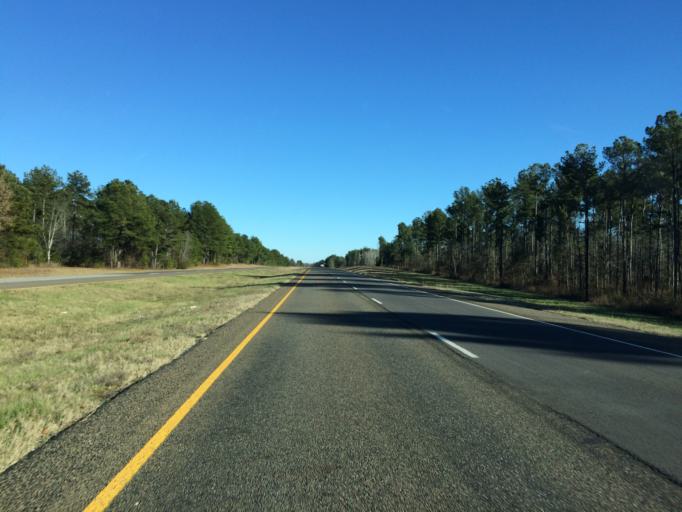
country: US
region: Texas
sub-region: Wood County
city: Hawkins
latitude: 32.6008
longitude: -95.2689
